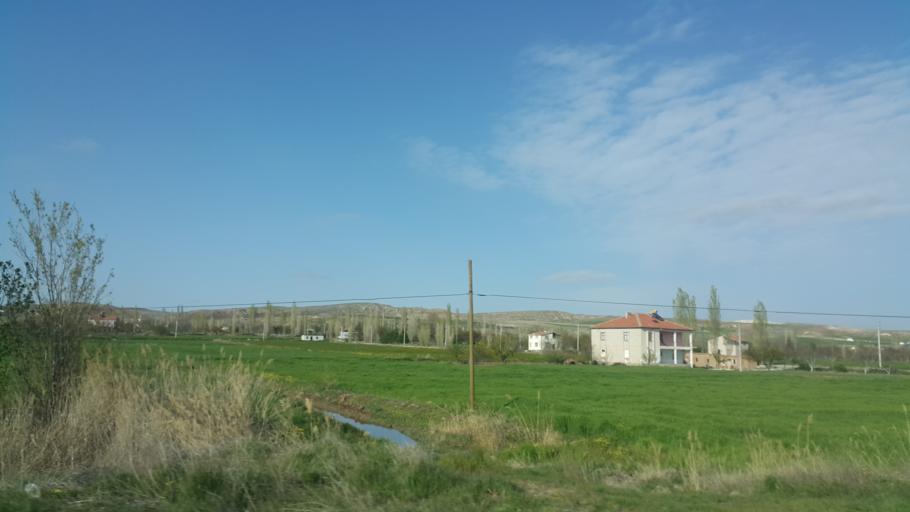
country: TR
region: Aksaray
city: Acipinar
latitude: 38.4864
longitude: 33.8838
